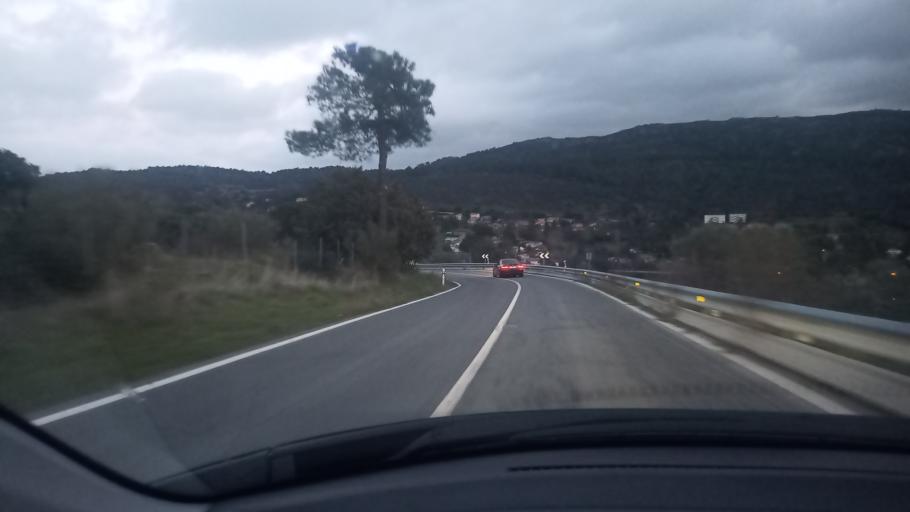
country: ES
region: Madrid
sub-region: Provincia de Madrid
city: Robledo de Chavela
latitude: 40.5089
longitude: -4.2403
